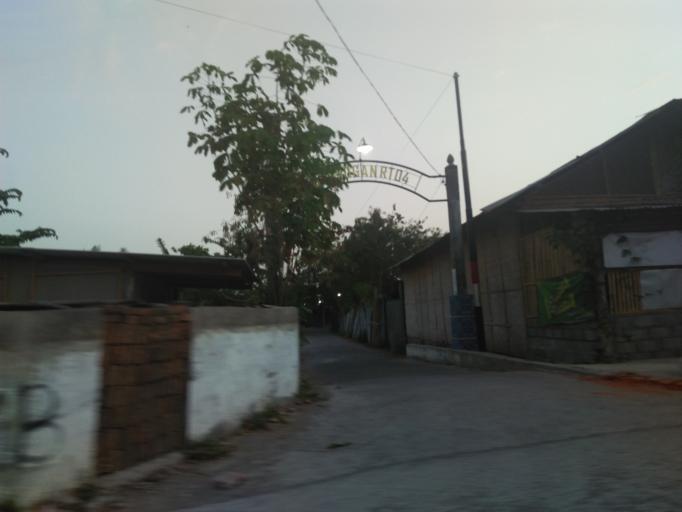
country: ID
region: Daerah Istimewa Yogyakarta
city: Sewon
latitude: -7.8436
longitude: 110.3933
